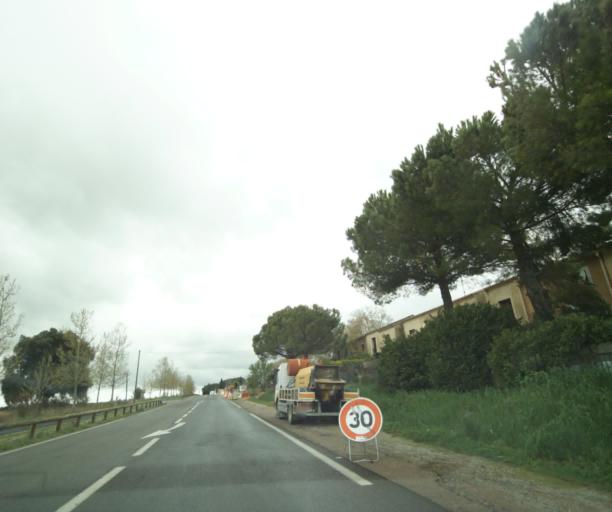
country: FR
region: Languedoc-Roussillon
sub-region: Departement de l'Herault
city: Cournonsec
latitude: 43.5473
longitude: 3.7074
